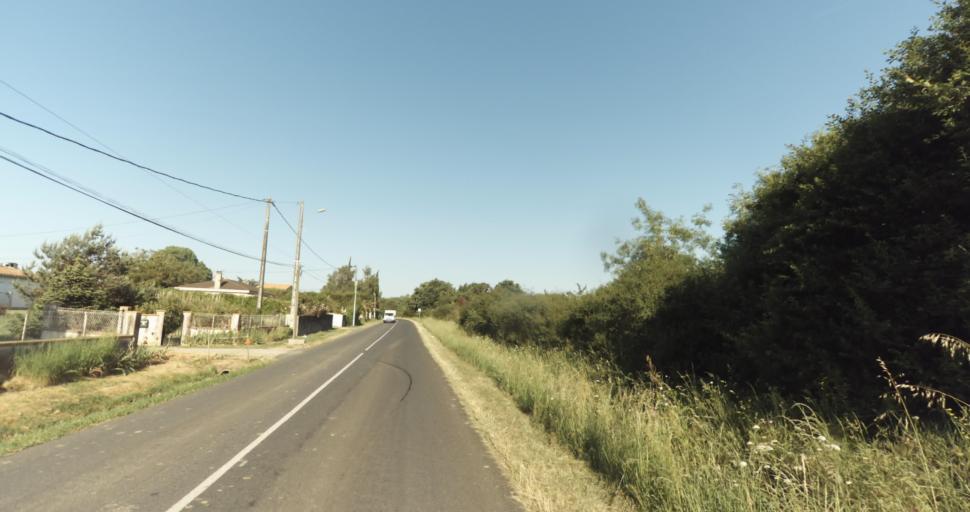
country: FR
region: Midi-Pyrenees
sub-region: Departement de la Haute-Garonne
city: Fonsorbes
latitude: 43.5675
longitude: 1.2272
